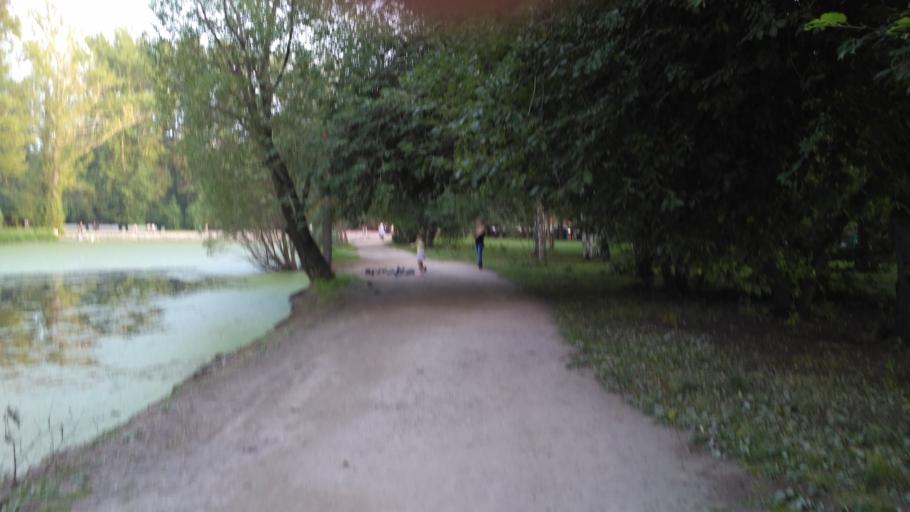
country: RU
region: Sverdlovsk
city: Yekaterinburg
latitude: 56.8476
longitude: 60.6494
